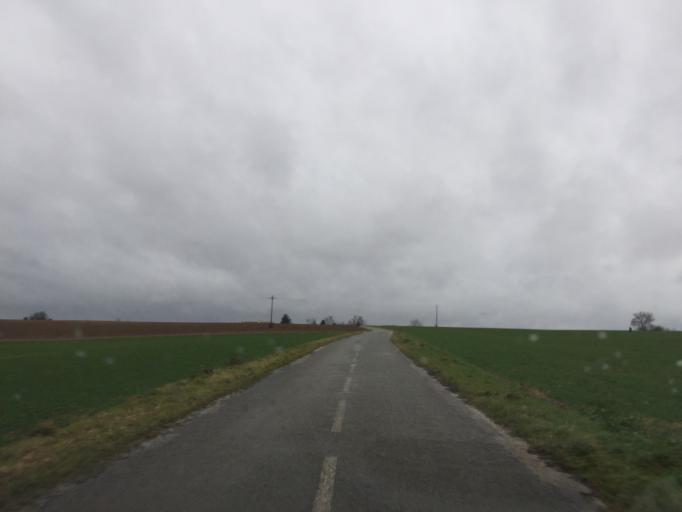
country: FR
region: Franche-Comte
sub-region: Departement du Jura
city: Dole
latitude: 47.1586
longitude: 5.5061
